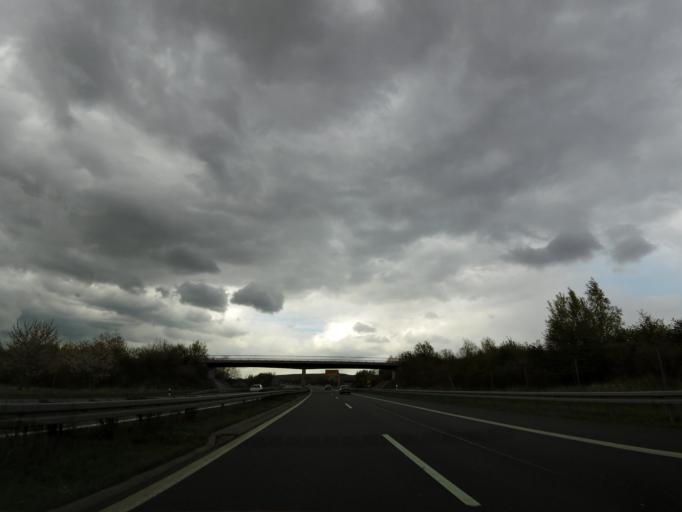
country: DE
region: Saxony-Anhalt
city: Darlingerode
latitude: 51.8732
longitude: 10.7526
